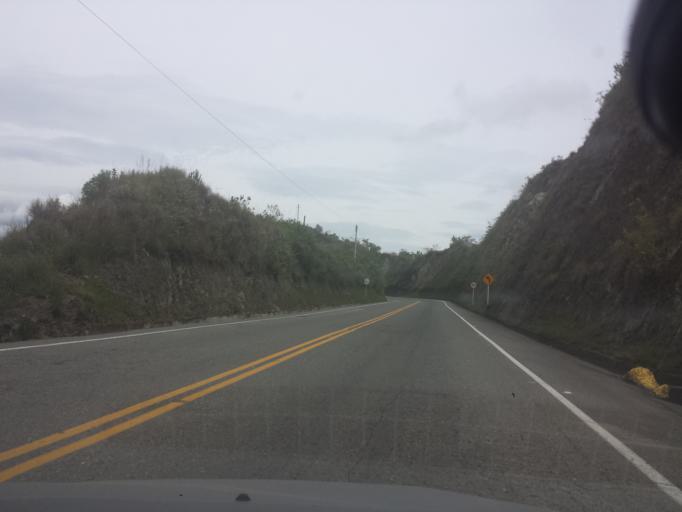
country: CO
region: Antioquia
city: Antioquia
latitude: 6.6056
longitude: -75.8604
